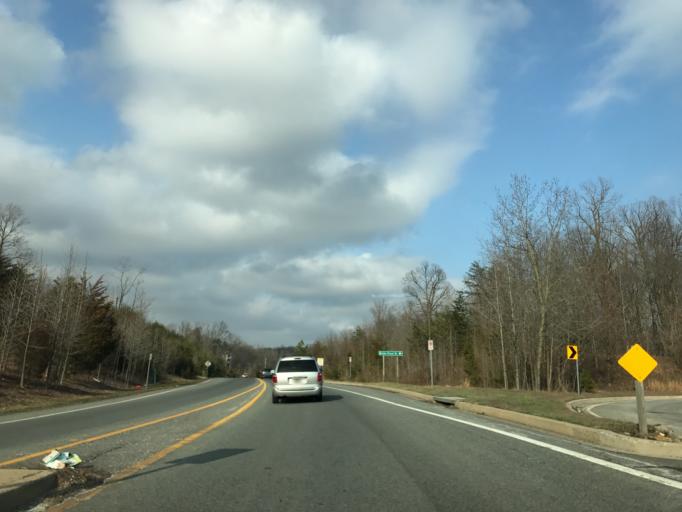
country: US
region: Maryland
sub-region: Harford County
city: Riverside
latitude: 39.4823
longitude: -76.2439
